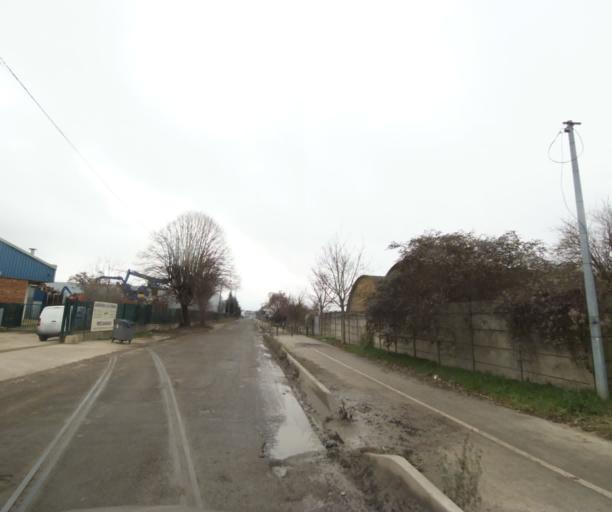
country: FR
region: Ile-de-France
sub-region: Departement du Val-de-Marne
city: Ablon-sur-Seine
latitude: 48.7354
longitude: 2.4298
